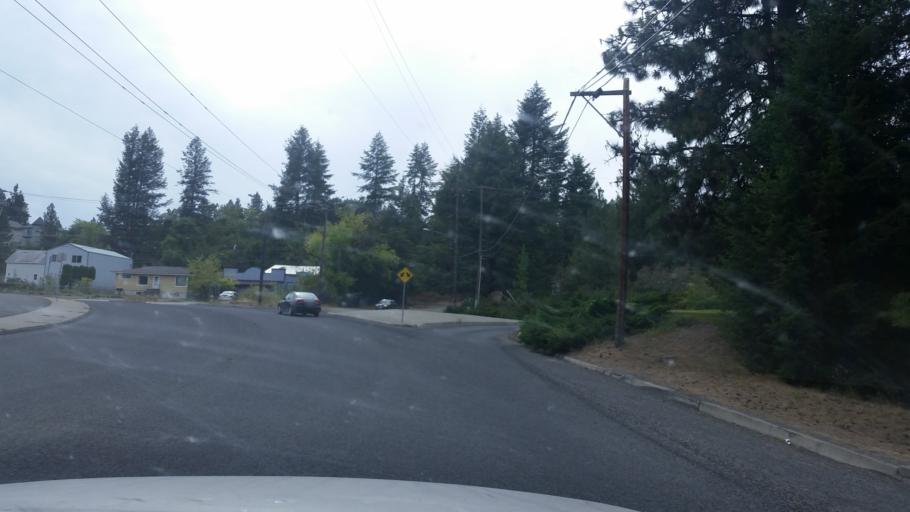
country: US
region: Washington
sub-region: Spokane County
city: Spokane
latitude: 47.6570
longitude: -117.4648
